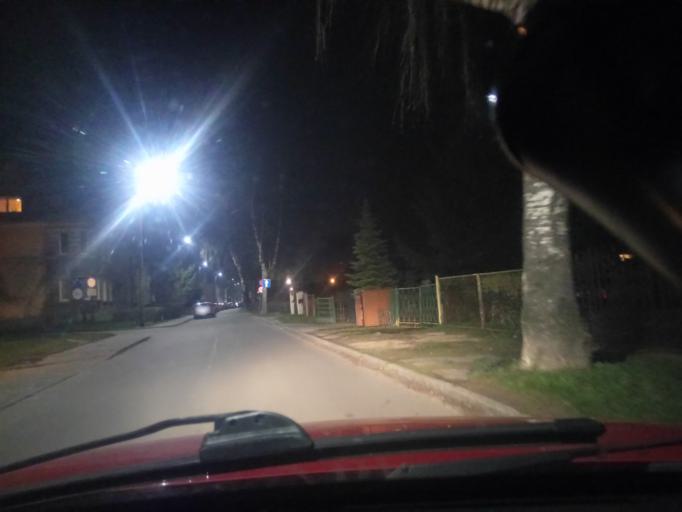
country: PL
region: Warmian-Masurian Voivodeship
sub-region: Powiat elblaski
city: Elblag
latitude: 54.1799
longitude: 19.4118
